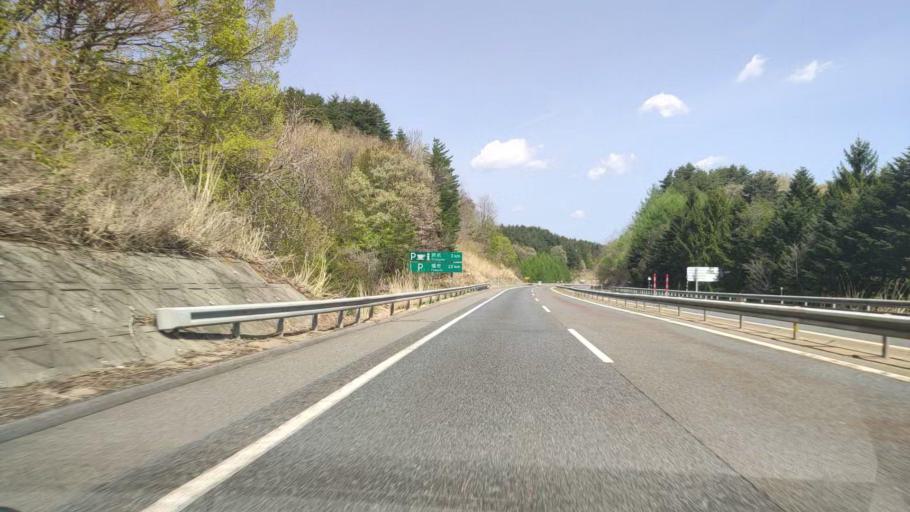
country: JP
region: Iwate
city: Ichinohe
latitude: 40.2704
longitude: 141.3992
